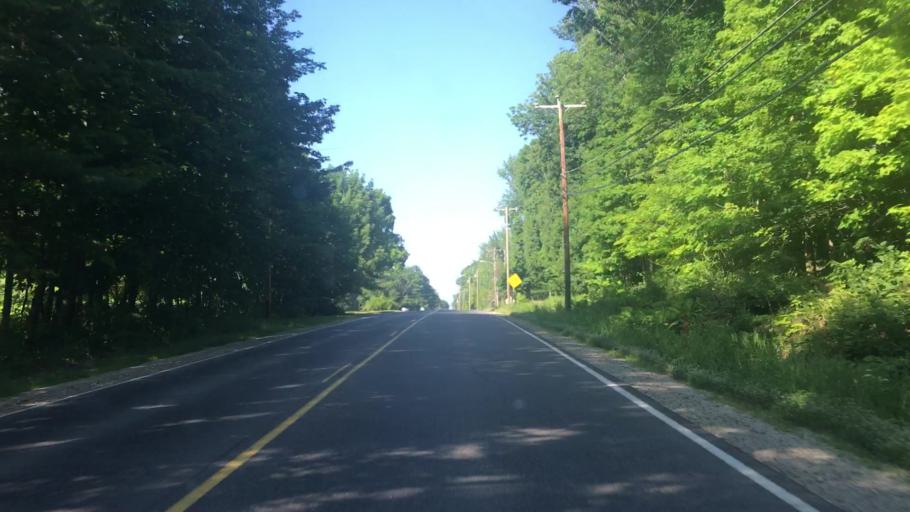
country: US
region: Maine
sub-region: York County
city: Buxton
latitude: 43.7439
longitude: -70.5425
